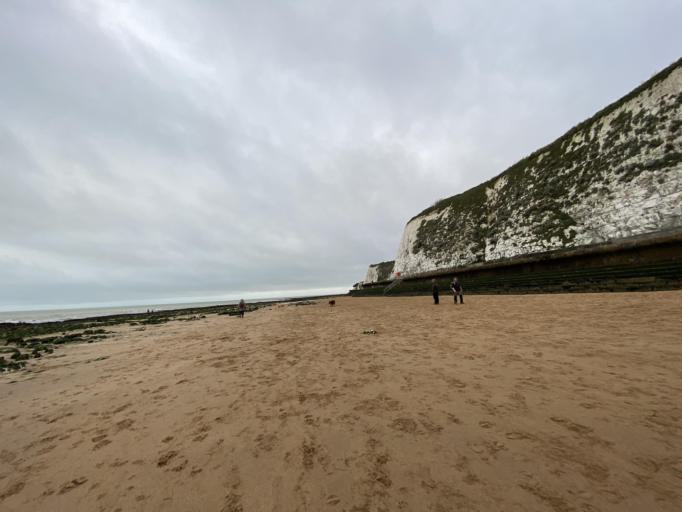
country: GB
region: England
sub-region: Kent
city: Broadstairs
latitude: 51.3506
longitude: 1.4427
